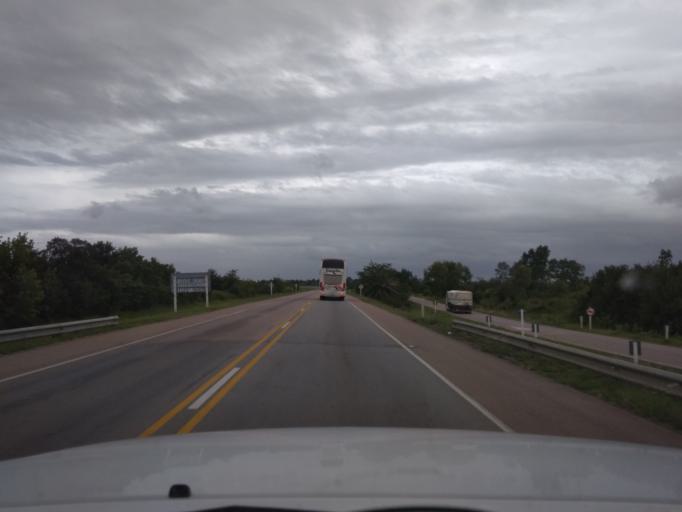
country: UY
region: Canelones
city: Canelones
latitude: -34.4995
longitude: -56.2819
